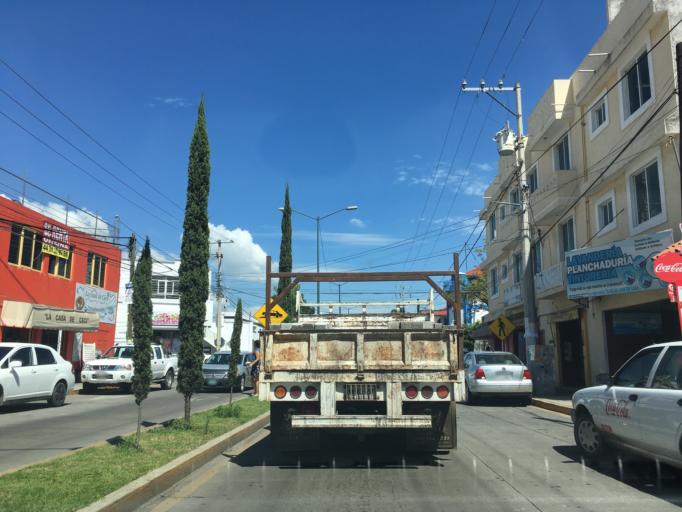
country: MX
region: Michoacan
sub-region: Morelia
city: Morelos
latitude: 19.6810
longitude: -101.2257
